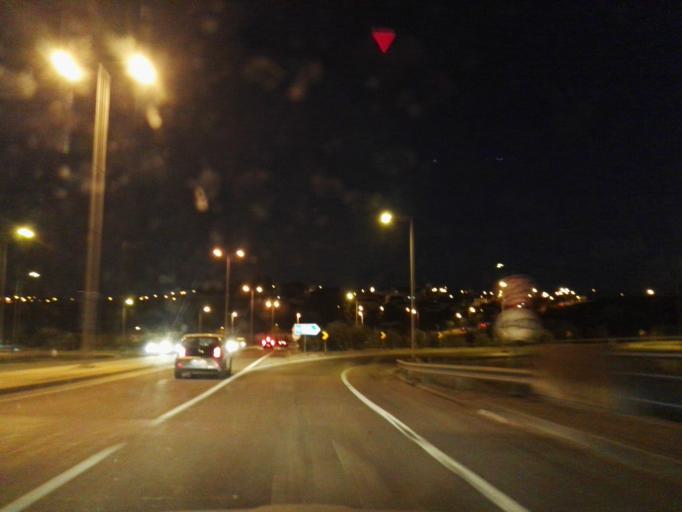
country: PT
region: Setubal
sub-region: Almada
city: Sobreda
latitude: 38.6607
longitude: -9.1891
